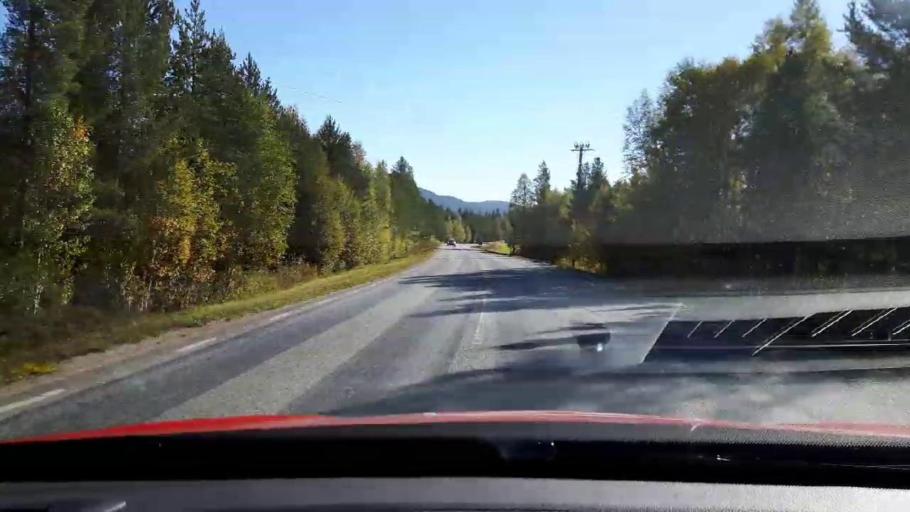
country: SE
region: Jaemtland
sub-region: Harjedalens Kommun
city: Sveg
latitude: 62.3636
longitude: 13.9978
